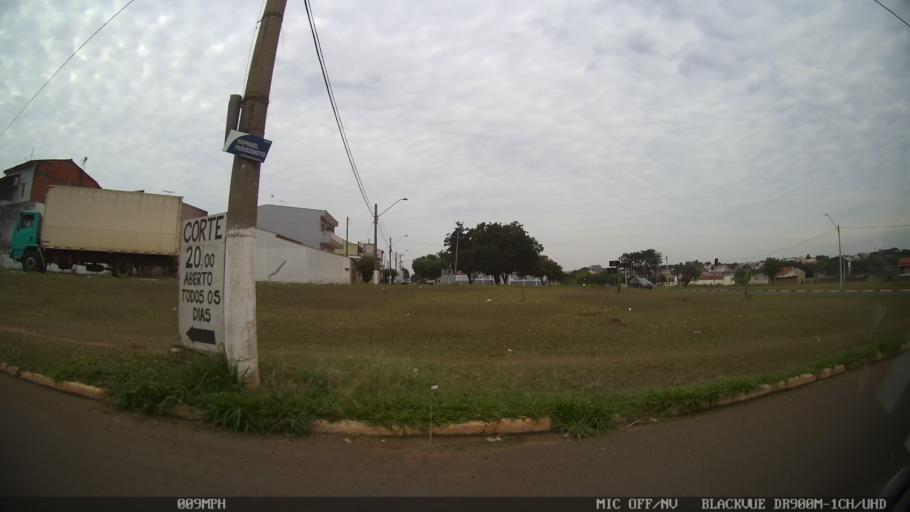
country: BR
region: Sao Paulo
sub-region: Paulinia
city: Paulinia
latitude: -22.7234
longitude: -47.1818
